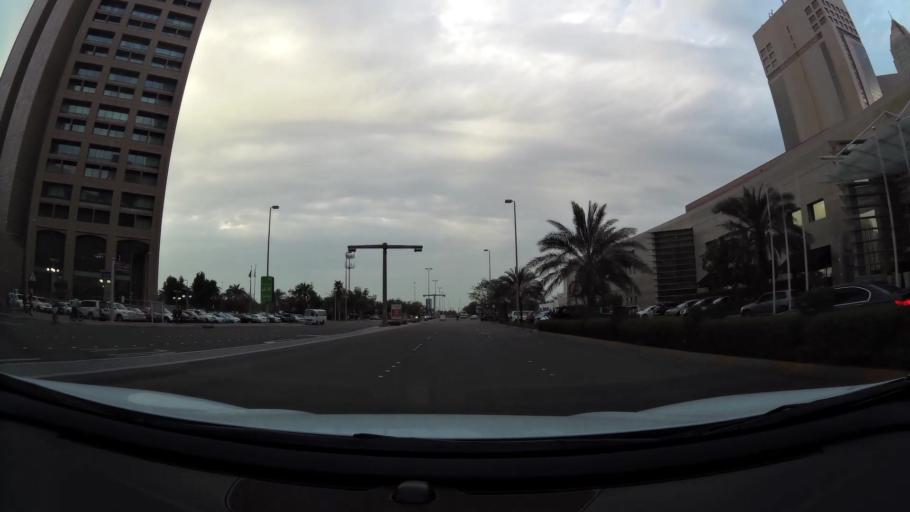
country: AE
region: Abu Dhabi
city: Abu Dhabi
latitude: 24.4960
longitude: 54.3653
